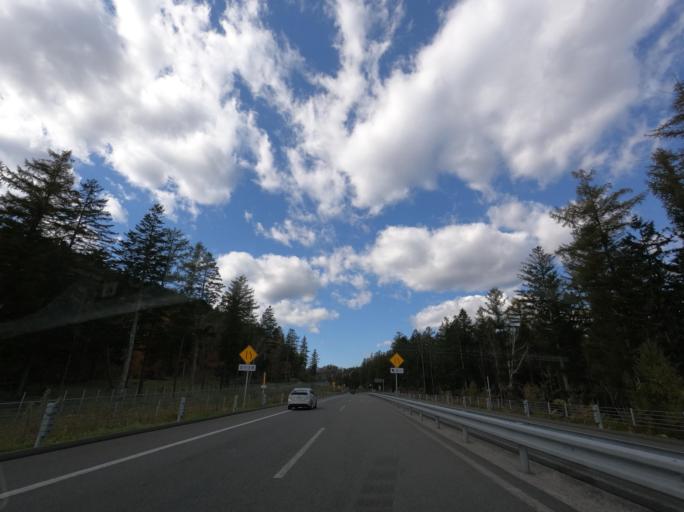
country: JP
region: Hokkaido
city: Kushiro
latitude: 43.0790
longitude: 144.0562
